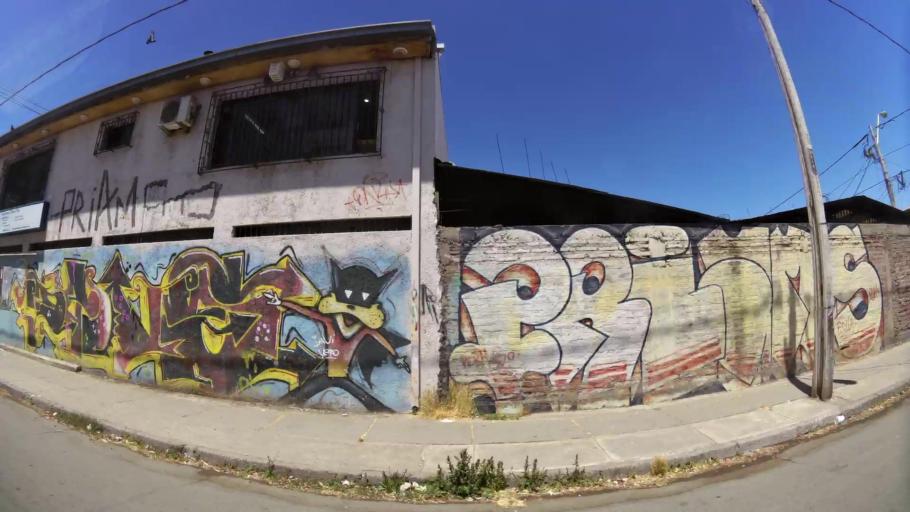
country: CL
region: Santiago Metropolitan
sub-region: Provincia de Santiago
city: La Pintana
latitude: -33.5740
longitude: -70.6668
